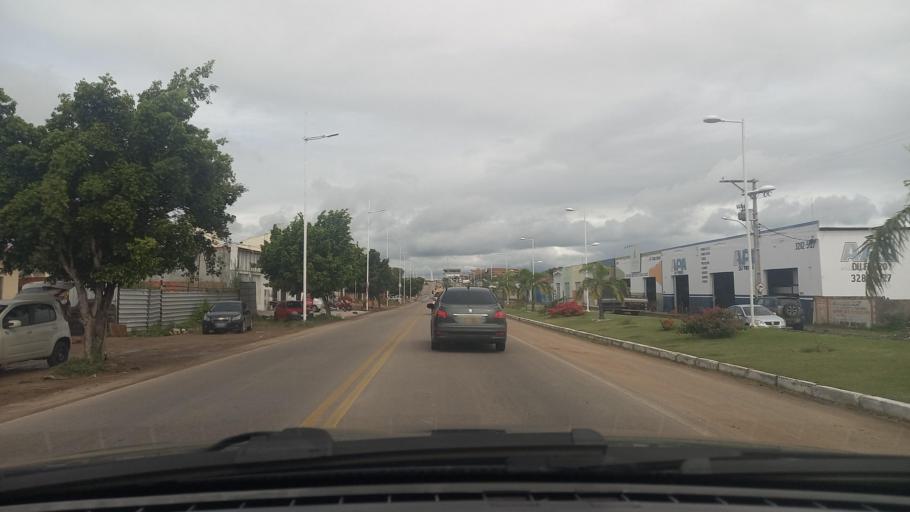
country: BR
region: Bahia
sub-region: Paulo Afonso
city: Paulo Afonso
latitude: -9.4420
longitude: -38.2235
